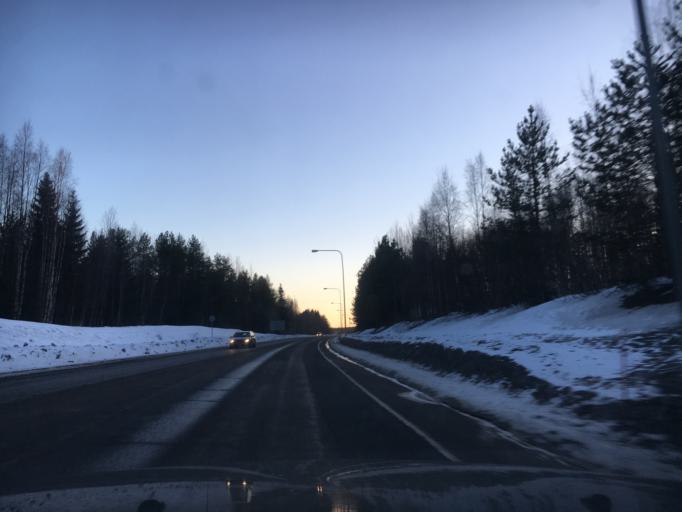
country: FI
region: Kainuu
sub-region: Kajaani
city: Kajaani
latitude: 64.2313
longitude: 27.7903
